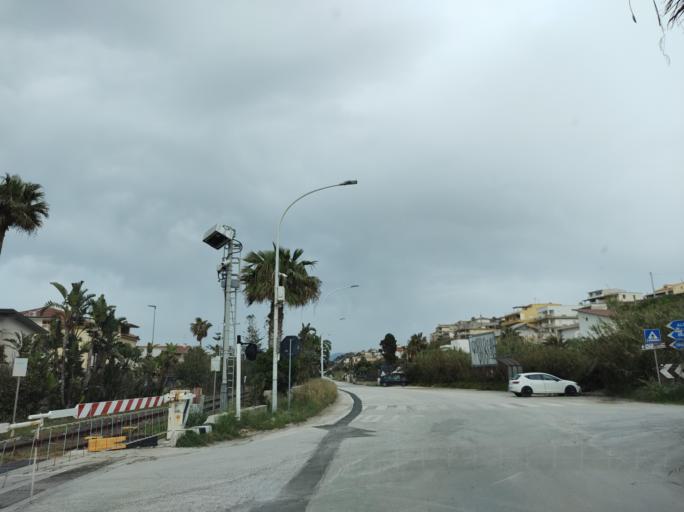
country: IT
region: Sicily
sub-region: Trapani
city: Castellammare del Golfo
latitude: 38.0252
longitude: 12.9198
